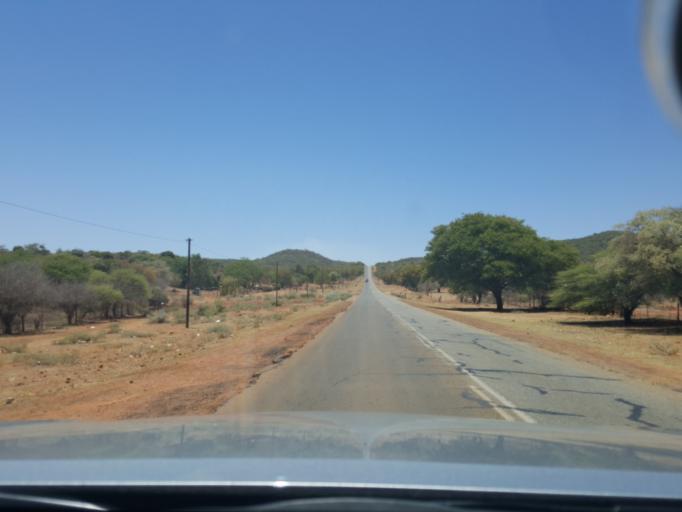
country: BW
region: South East
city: Lobatse
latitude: -25.3041
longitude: 25.9281
